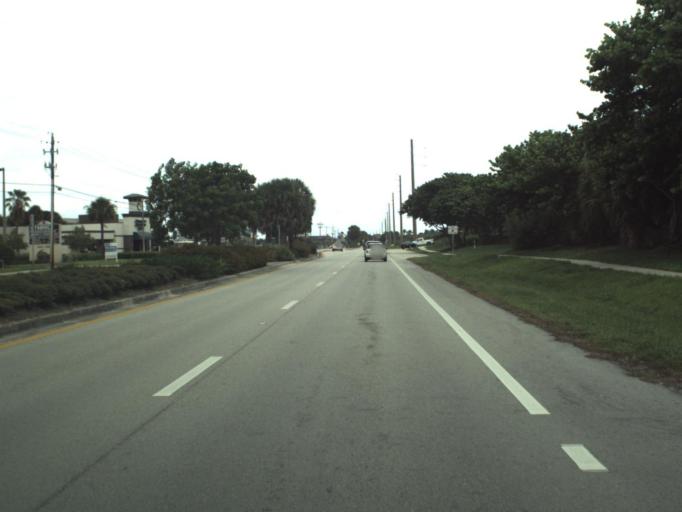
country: US
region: Florida
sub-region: Palm Beach County
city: Juno Beach
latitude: 26.8832
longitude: -80.0568
